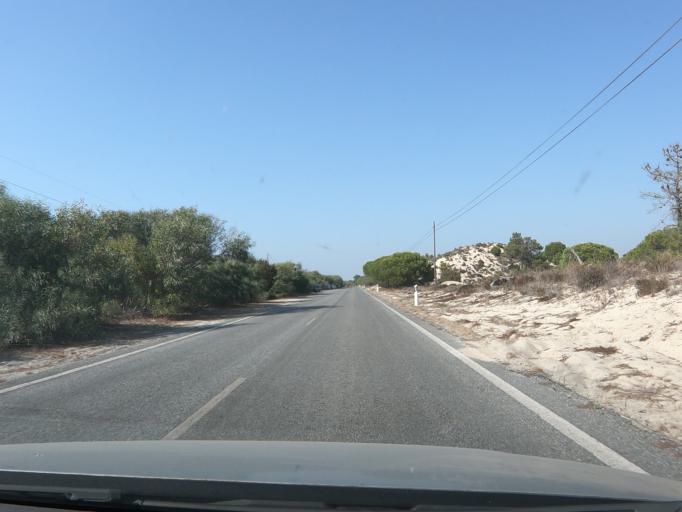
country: PT
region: Setubal
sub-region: Setubal
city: Setubal
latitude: 38.3983
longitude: -8.8056
